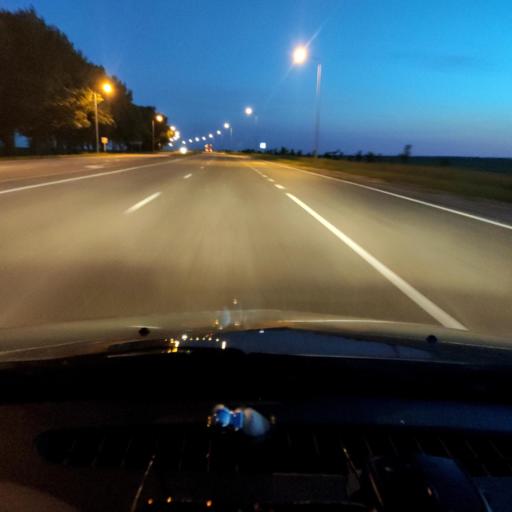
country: RU
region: Belgorod
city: Skorodnoye
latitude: 51.1726
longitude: 37.3234
